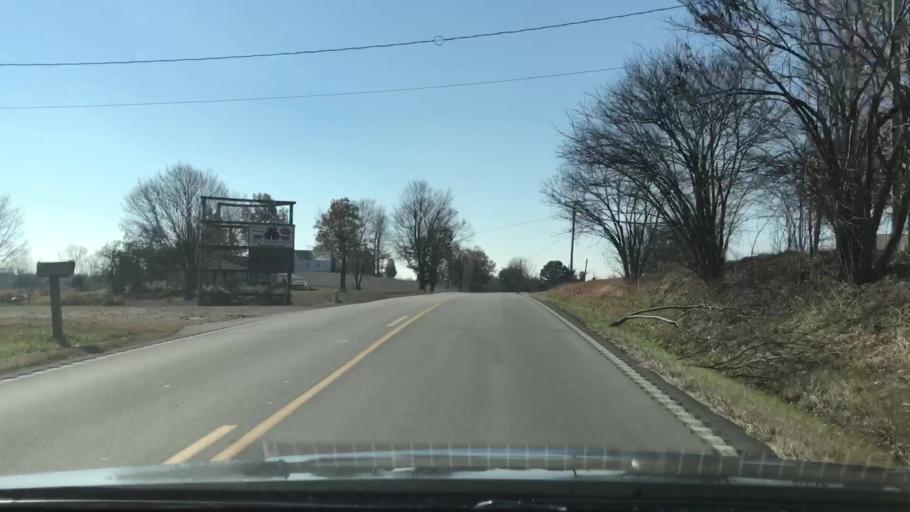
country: US
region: Kentucky
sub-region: Edmonson County
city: Brownsville
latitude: 37.3193
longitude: -86.2699
